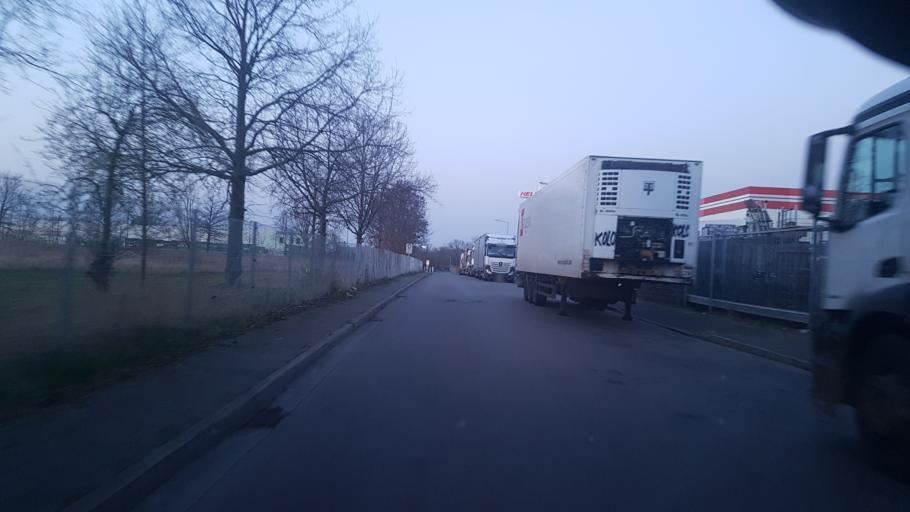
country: DE
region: Brandenburg
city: Ahrensfelde
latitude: 52.5974
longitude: 13.5993
